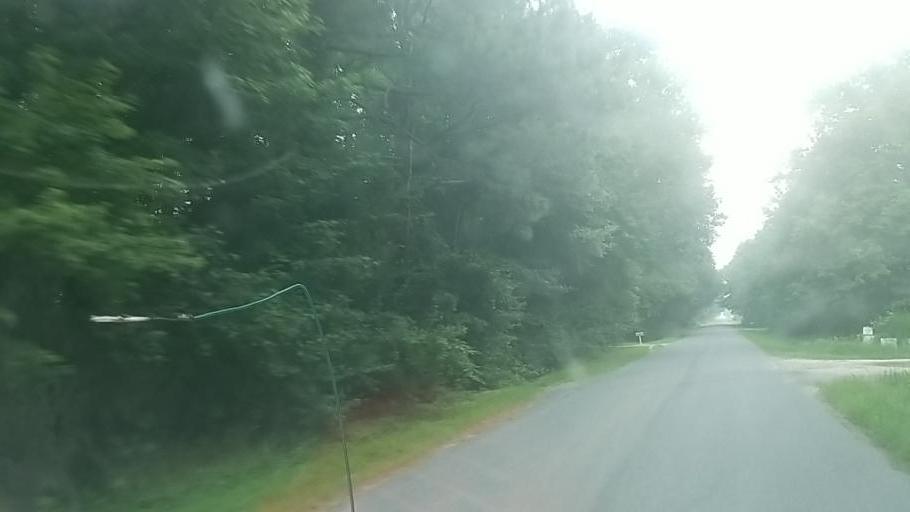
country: US
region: Maryland
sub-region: Wicomico County
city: Pittsville
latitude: 38.4521
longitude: -75.3815
